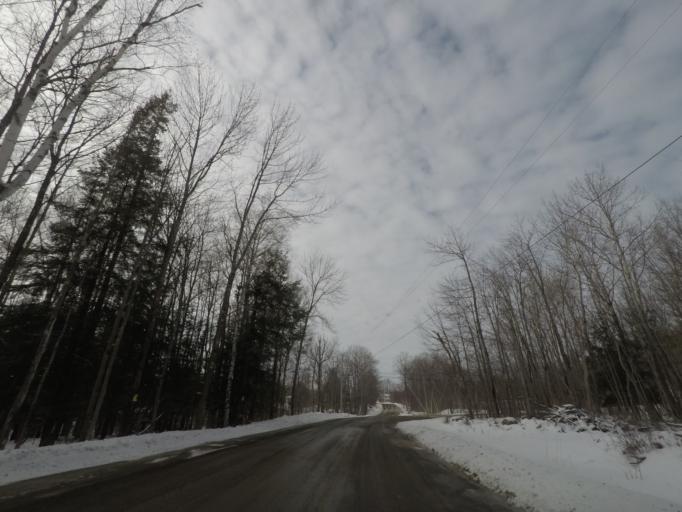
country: US
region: New York
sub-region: Rensselaer County
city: Averill Park
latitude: 42.6079
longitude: -73.4876
